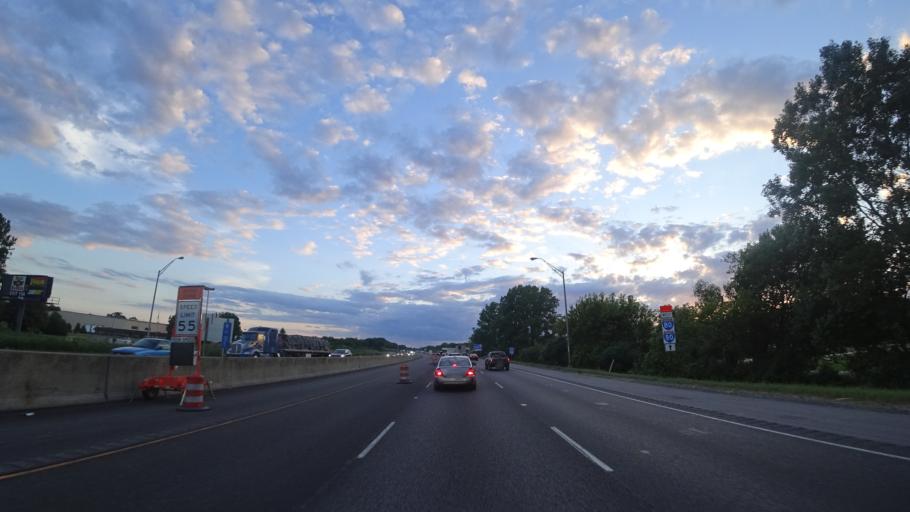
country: US
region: Indiana
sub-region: Porter County
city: Ogden Dunes
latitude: 41.6021
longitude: -87.1826
